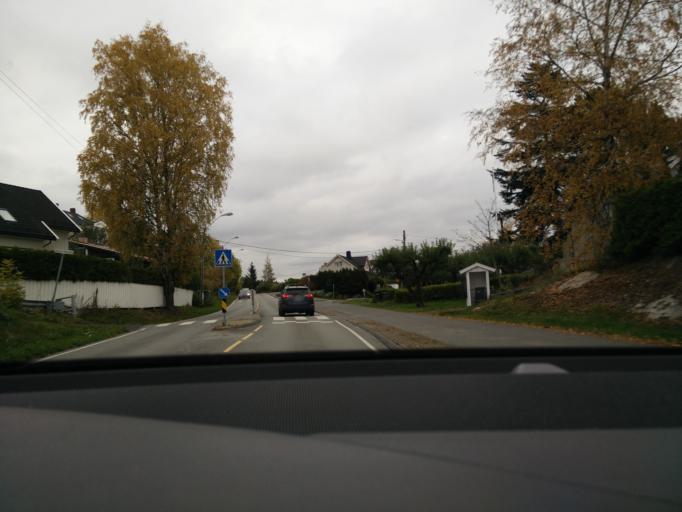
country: NO
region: Akershus
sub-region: Baerum
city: Lysaker
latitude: 59.9316
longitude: 10.6136
